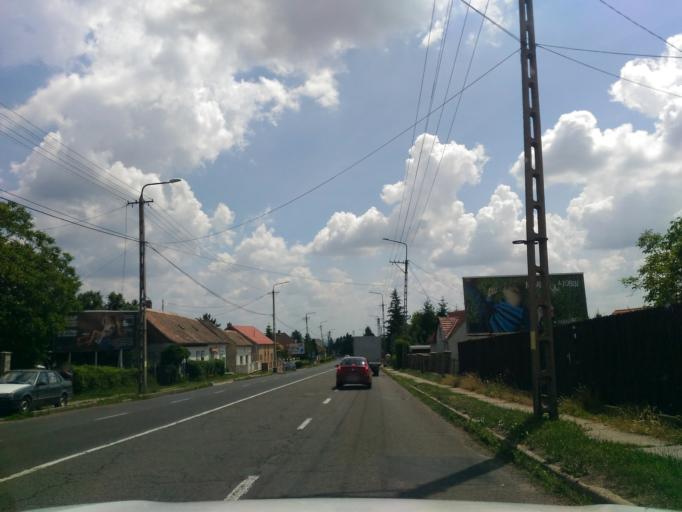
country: HU
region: Baranya
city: Pecs
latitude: 46.1136
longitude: 18.2618
